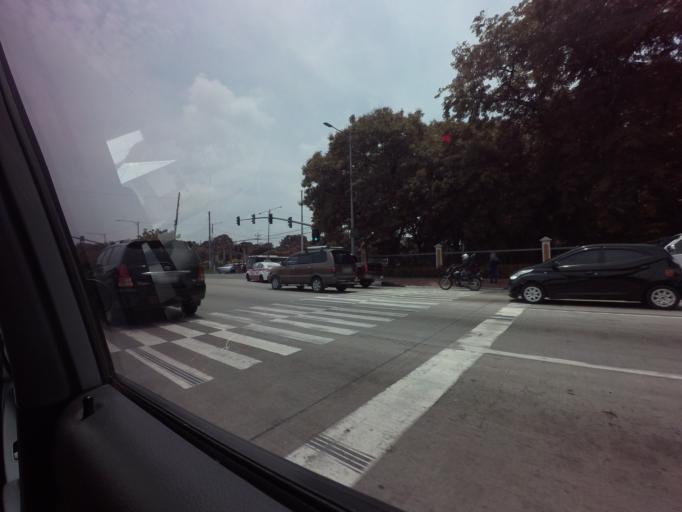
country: PH
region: Metro Manila
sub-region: City of Manila
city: Port Area
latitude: 14.5827
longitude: 120.9757
